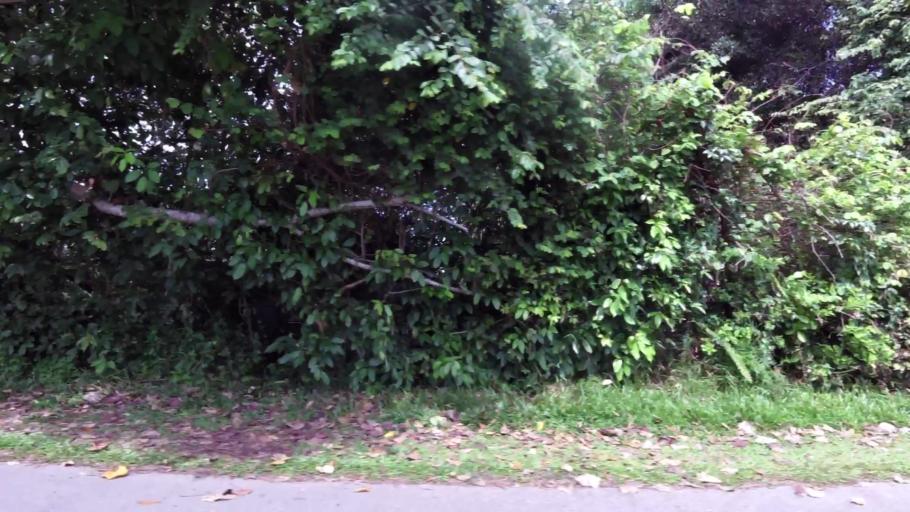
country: BN
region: Belait
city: Seria
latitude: 4.5980
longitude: 114.2829
